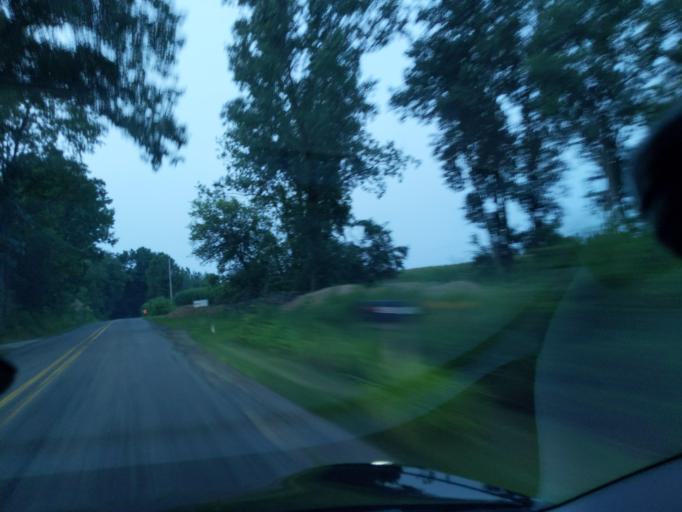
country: US
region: Michigan
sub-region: Ingham County
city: Leslie
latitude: 42.4525
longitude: -84.5508
